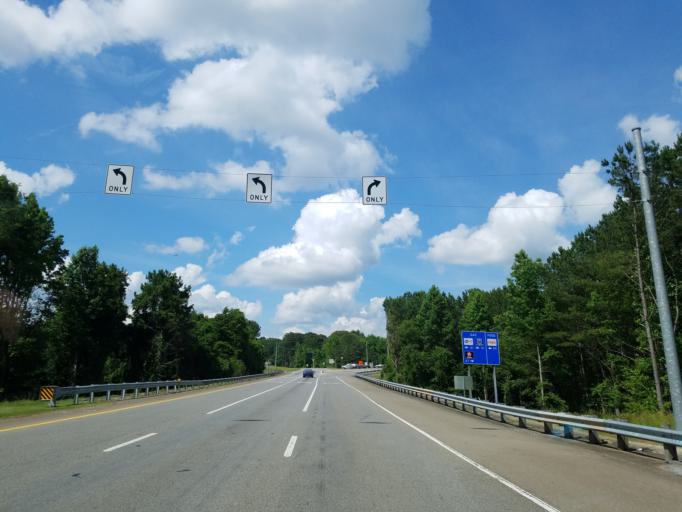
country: US
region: Georgia
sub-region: Cherokee County
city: Holly Springs
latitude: 34.1872
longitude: -84.5051
